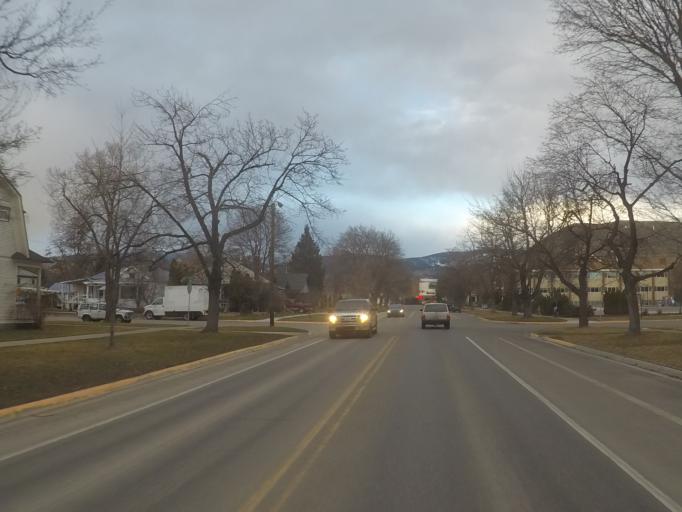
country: US
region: Montana
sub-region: Missoula County
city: Missoula
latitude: 46.8611
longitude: -114.0001
